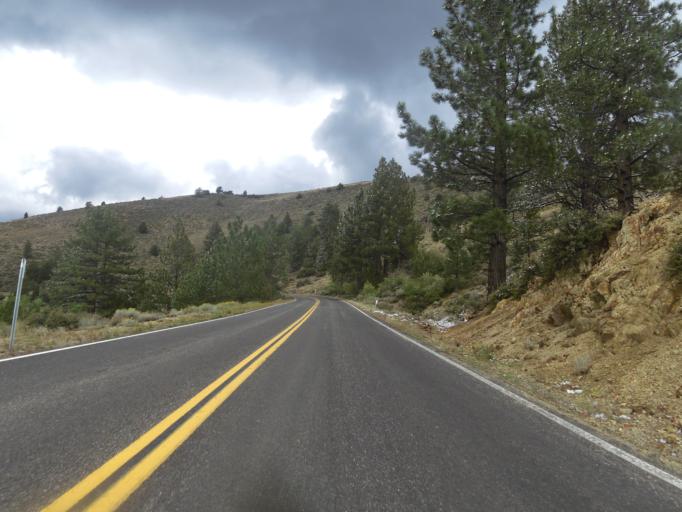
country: US
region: Nevada
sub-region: Douglas County
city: Gardnerville Ranchos
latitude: 38.6719
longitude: -119.6545
